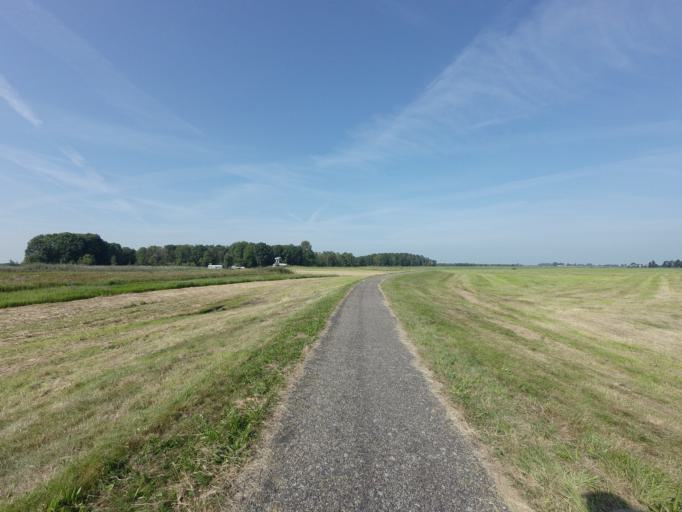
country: NL
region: Overijssel
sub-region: Gemeente Steenwijkerland
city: Oldemarkt
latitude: 52.8371
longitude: 5.9427
